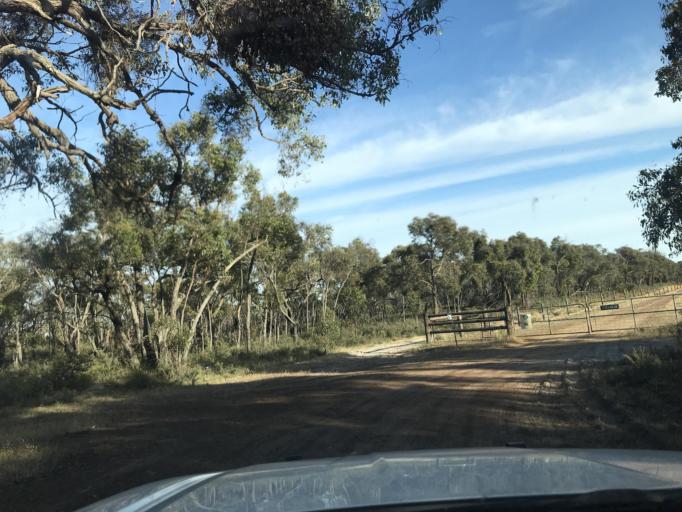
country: AU
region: South Australia
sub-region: Wattle Range
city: Penola
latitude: -37.0856
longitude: 141.4498
